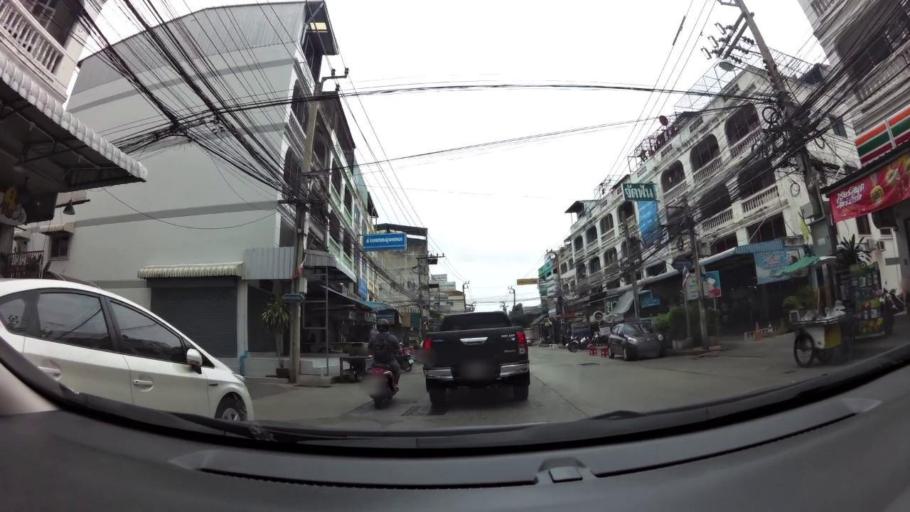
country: TH
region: Bangkok
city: Bang Na
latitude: 13.6800
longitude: 100.6370
